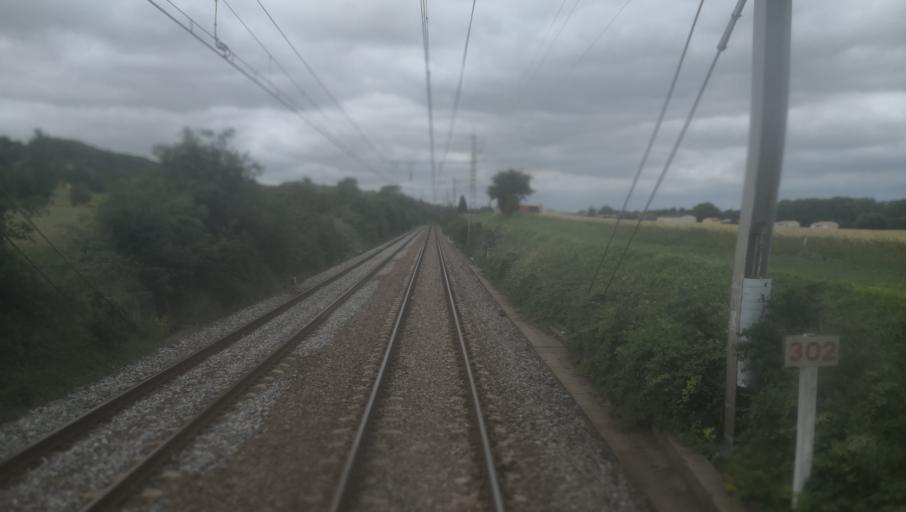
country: FR
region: Midi-Pyrenees
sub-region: Departement de la Haute-Garonne
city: Avignonet-Lauragais
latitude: 43.3351
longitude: 1.8424
